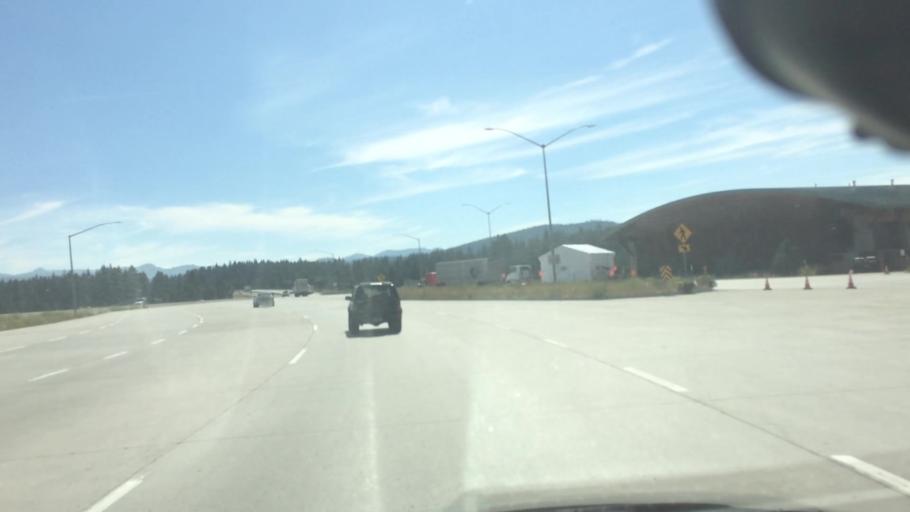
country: US
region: California
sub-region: Nevada County
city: Truckee
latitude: 39.3605
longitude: -120.1369
